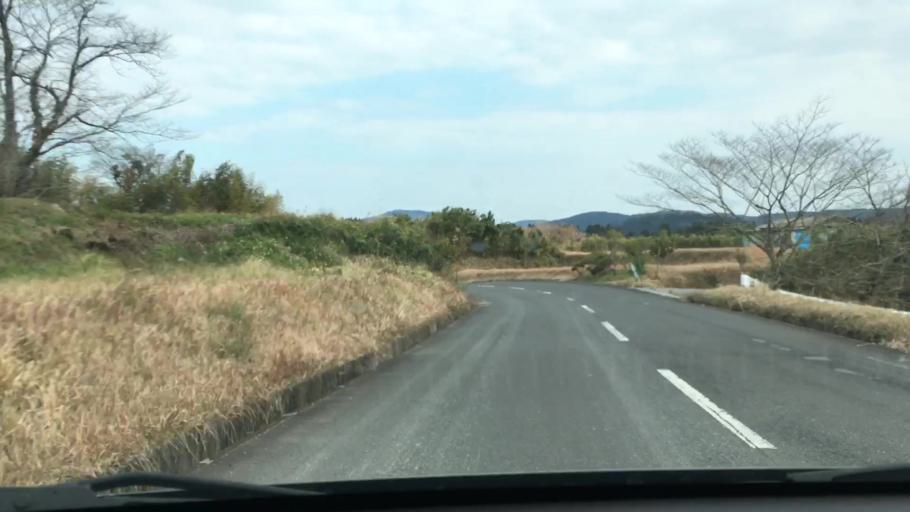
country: JP
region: Miyazaki
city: Kushima
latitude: 31.4963
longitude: 131.2353
